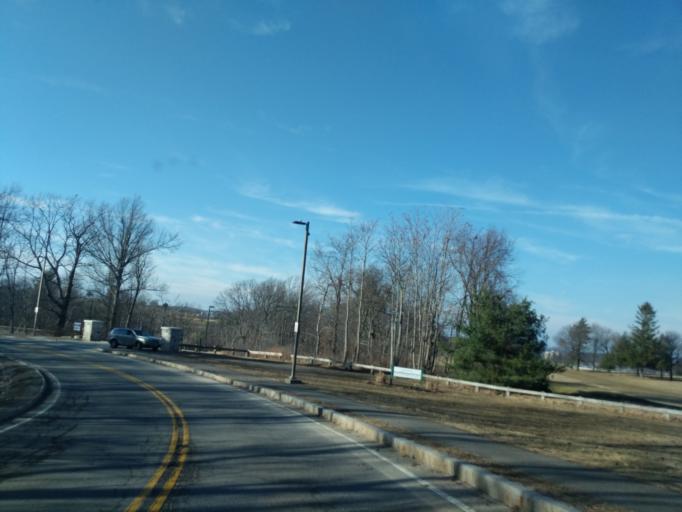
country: US
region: Massachusetts
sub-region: Worcester County
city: Hamilton
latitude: 42.2832
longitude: -71.7751
